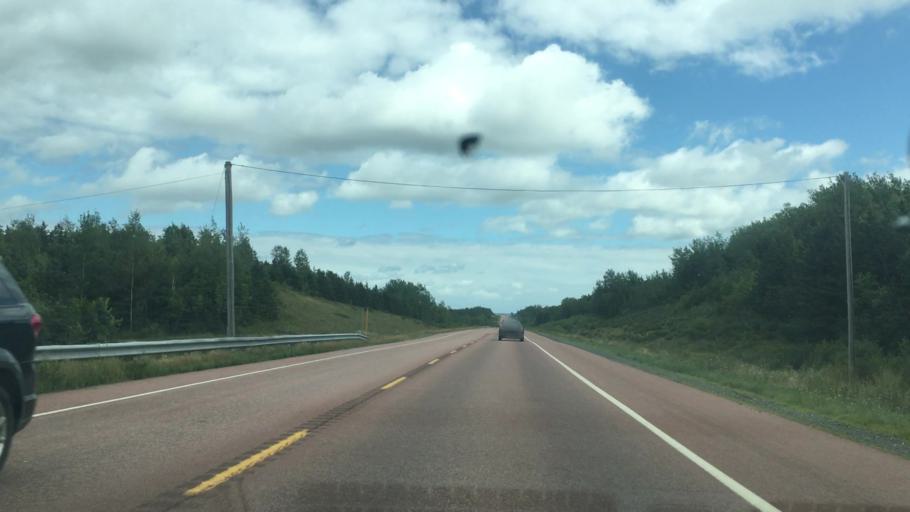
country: CA
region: Nova Scotia
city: Antigonish
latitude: 45.6037
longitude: -61.6903
